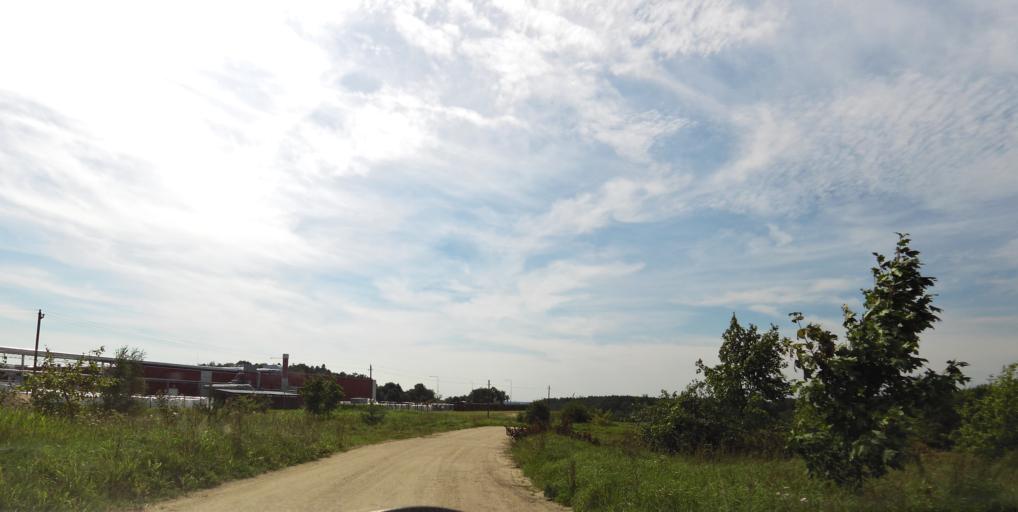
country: LT
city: Grigiskes
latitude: 54.7355
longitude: 25.0745
